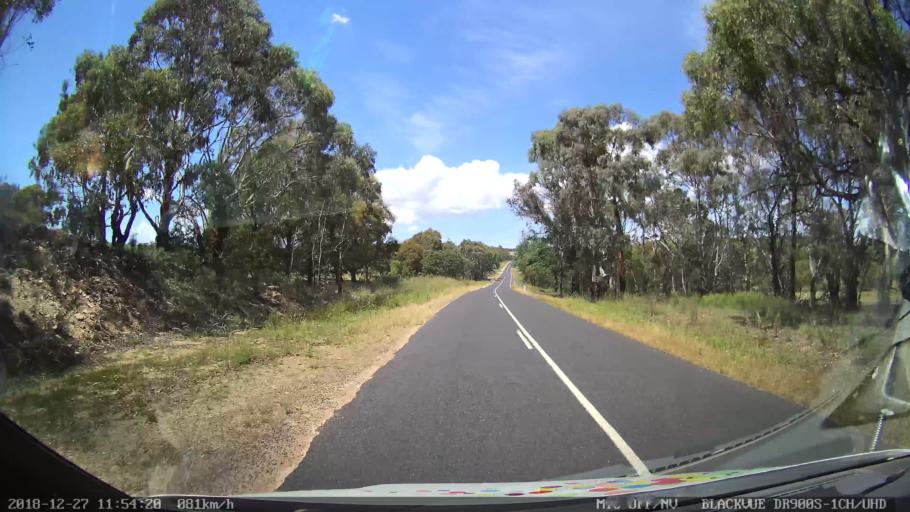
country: AU
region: New South Wales
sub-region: Blayney
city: Blayney
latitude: -33.6736
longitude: 149.4025
